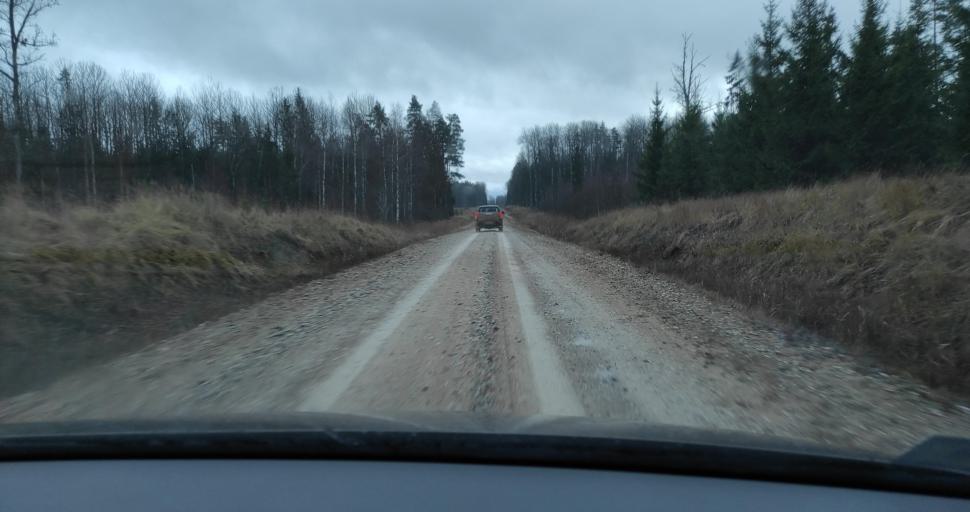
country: LV
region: Skrunda
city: Skrunda
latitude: 56.5627
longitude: 22.0791
